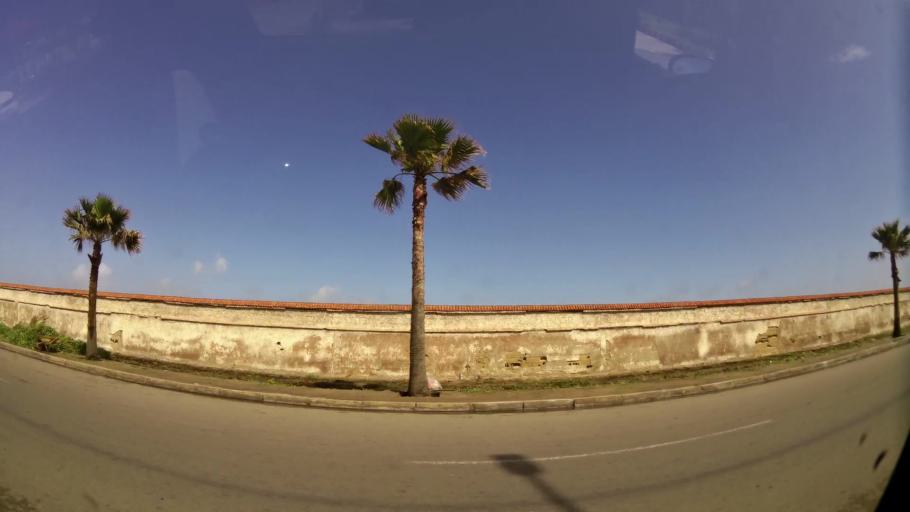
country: MA
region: Grand Casablanca
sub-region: Mediouna
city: Tit Mellil
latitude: 33.6219
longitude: -7.5287
